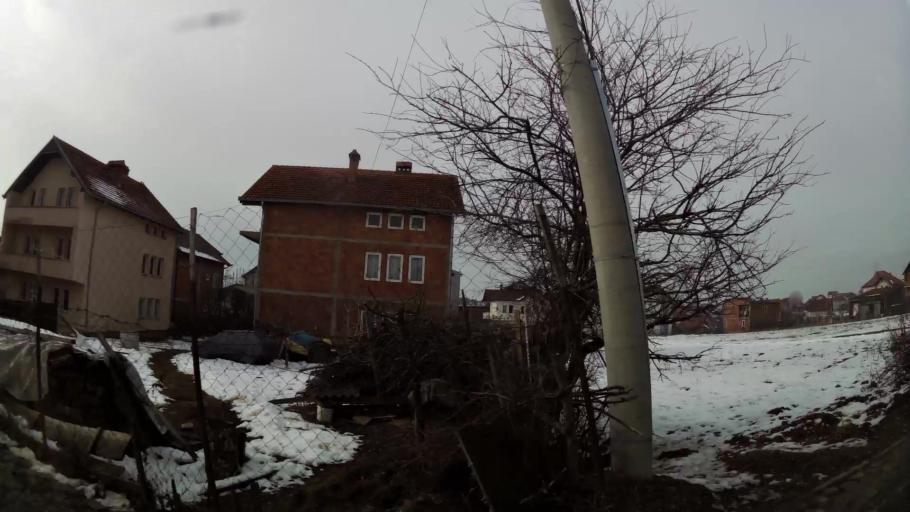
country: XK
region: Pristina
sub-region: Komuna e Prishtines
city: Pristina
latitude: 42.6879
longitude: 21.1657
